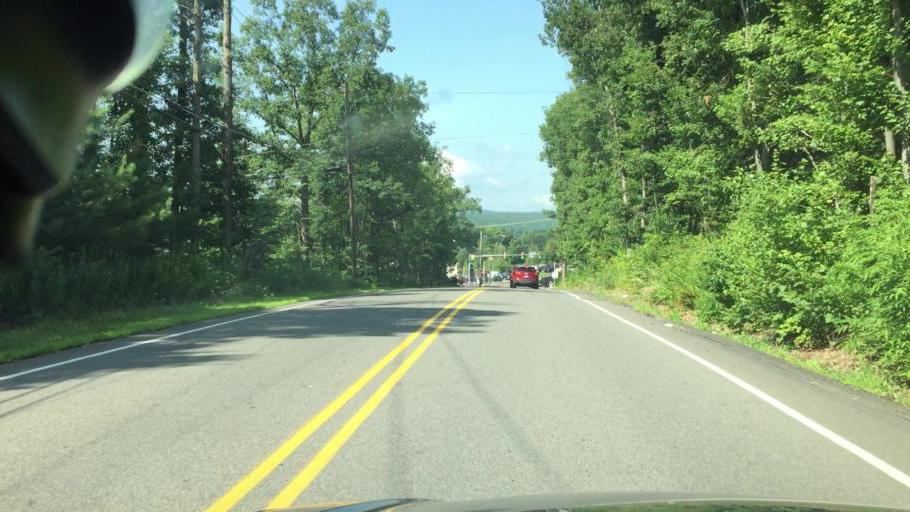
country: US
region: Pennsylvania
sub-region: Luzerne County
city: West Hazleton
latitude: 40.9778
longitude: -76.0162
